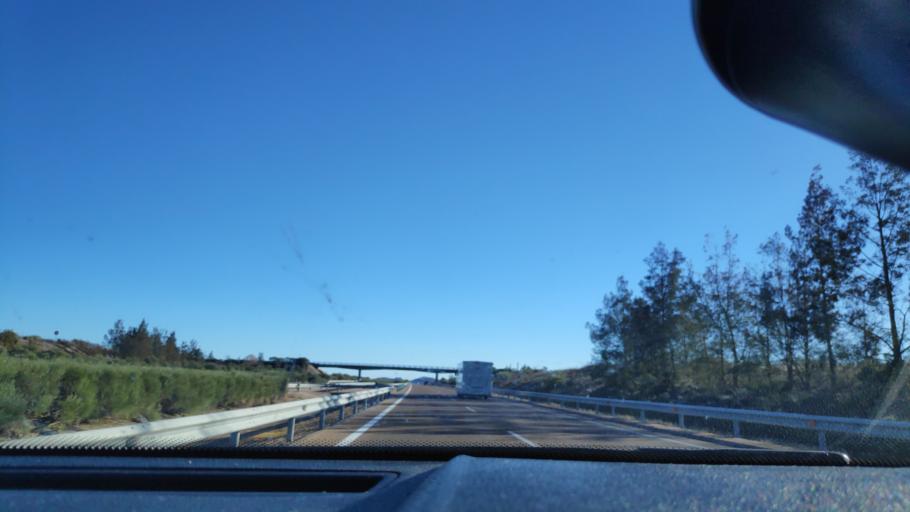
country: ES
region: Extremadura
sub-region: Provincia de Badajoz
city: Los Santos de Maimona
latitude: 38.4642
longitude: -6.3576
